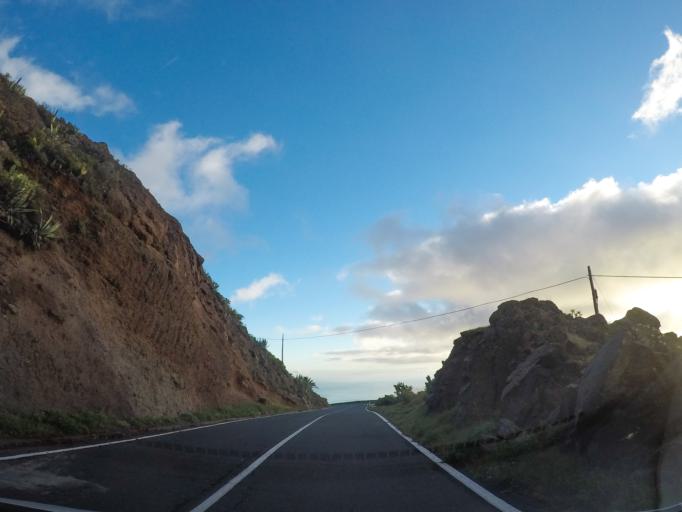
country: ES
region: Canary Islands
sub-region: Provincia de Santa Cruz de Tenerife
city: Alajero
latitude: 28.0786
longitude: -17.2430
